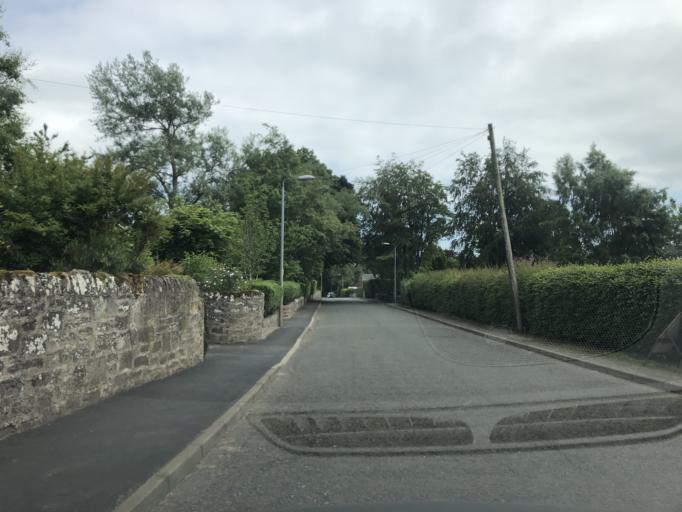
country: GB
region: Scotland
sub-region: Angus
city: Brechin
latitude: 56.7355
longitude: -2.6751
